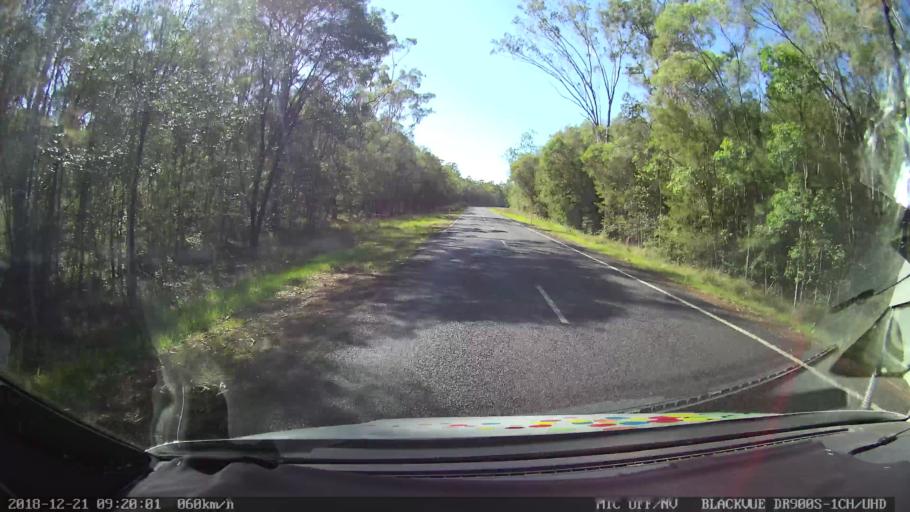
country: AU
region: New South Wales
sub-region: Clarence Valley
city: Maclean
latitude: -29.3107
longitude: 152.9984
